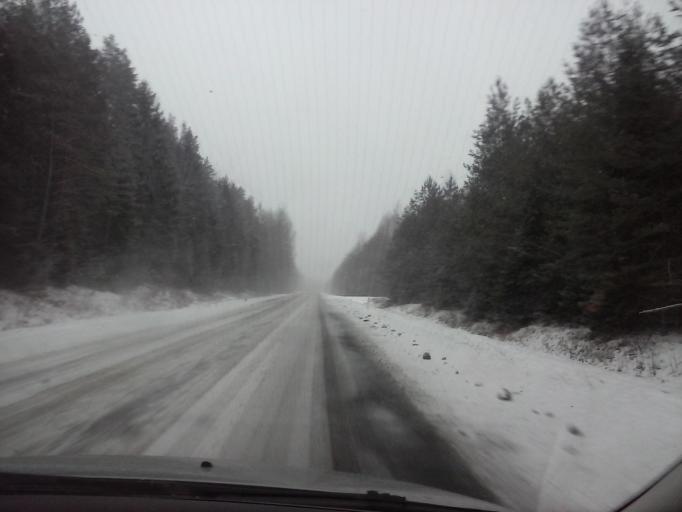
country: LV
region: Valkas Rajons
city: Valka
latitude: 57.7237
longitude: 25.9354
